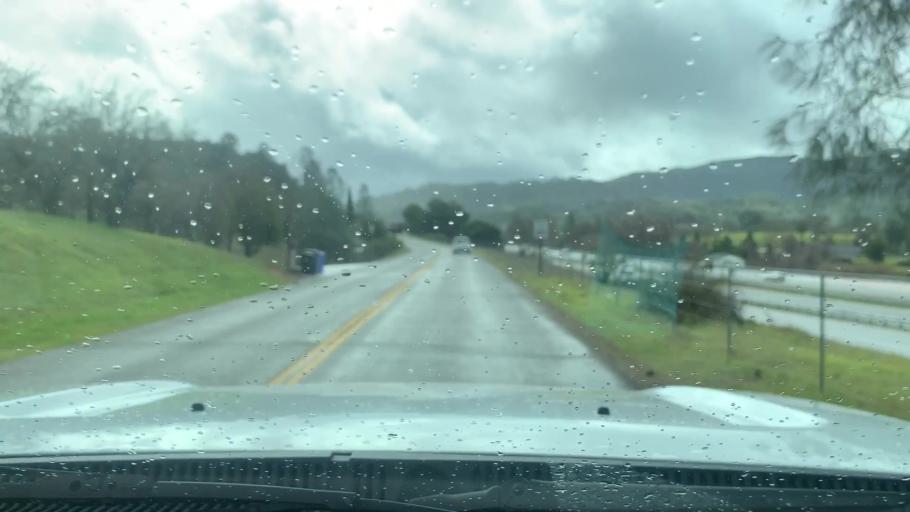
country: US
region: California
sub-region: San Luis Obispo County
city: Atascadero
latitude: 35.4431
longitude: -120.6370
